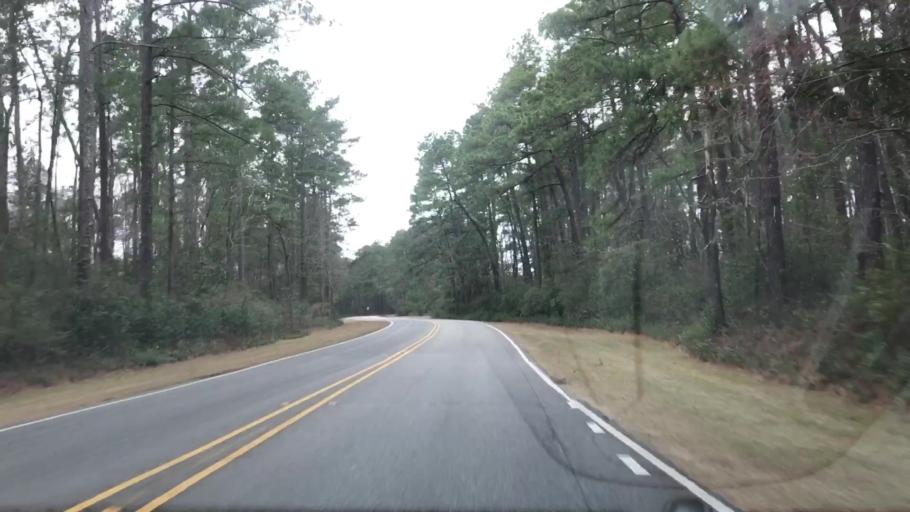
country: US
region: South Carolina
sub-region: Horry County
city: Red Hill
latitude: 33.7814
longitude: -78.9922
